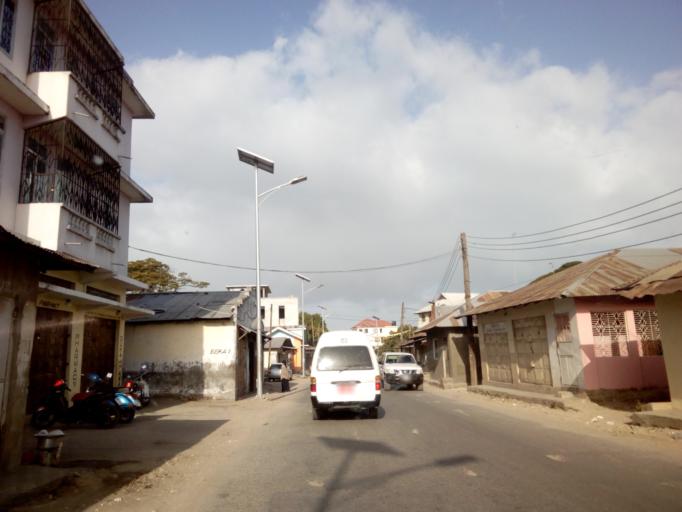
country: TZ
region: Zanzibar Urban/West
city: Zanzibar
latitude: -6.1623
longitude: 39.2060
